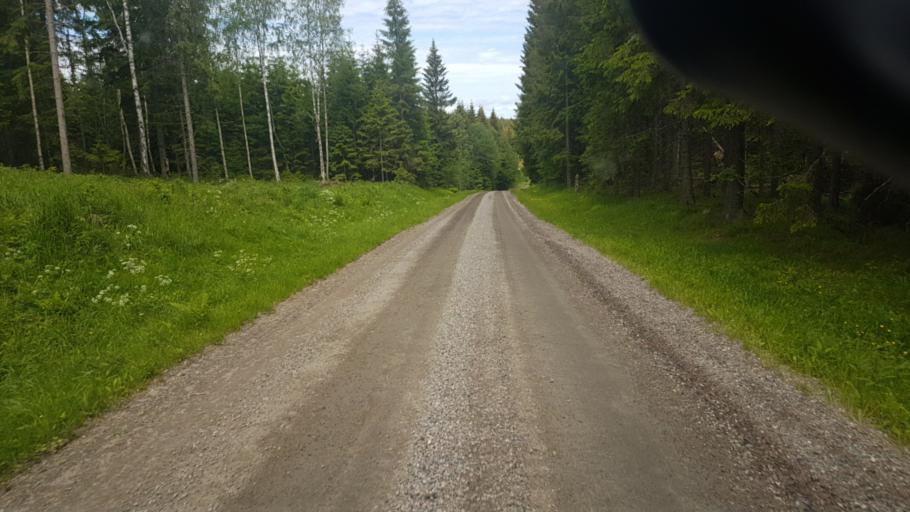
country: SE
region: Vaermland
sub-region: Eda Kommun
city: Charlottenberg
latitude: 60.0139
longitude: 12.5054
